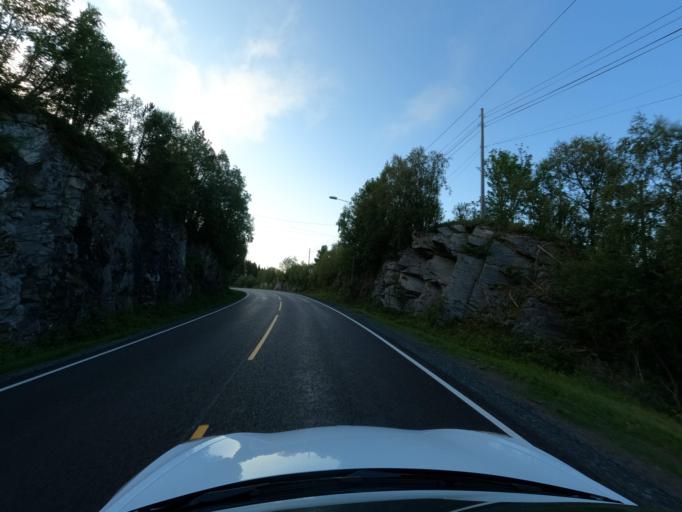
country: NO
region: Troms
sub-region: Skanland
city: Evenskjer
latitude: 68.6693
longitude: 16.5756
